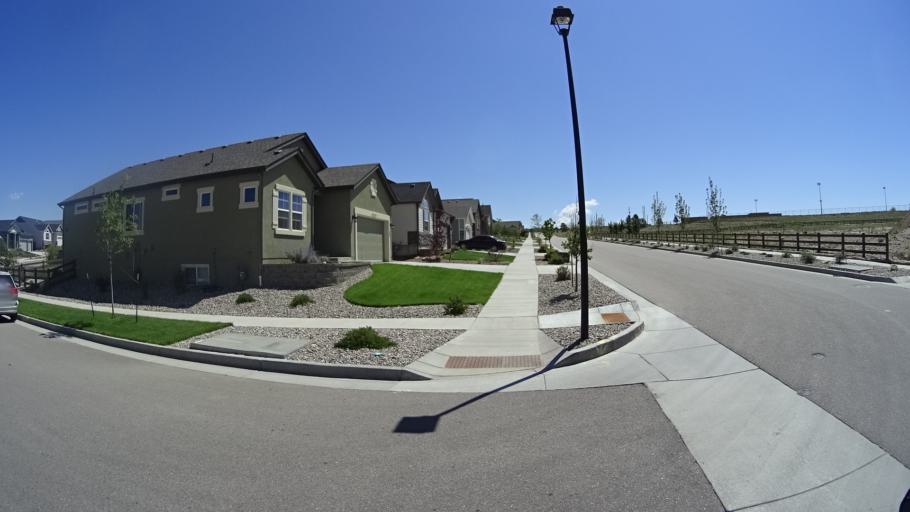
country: US
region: Colorado
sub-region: El Paso County
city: Black Forest
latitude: 38.9892
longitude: -104.7677
